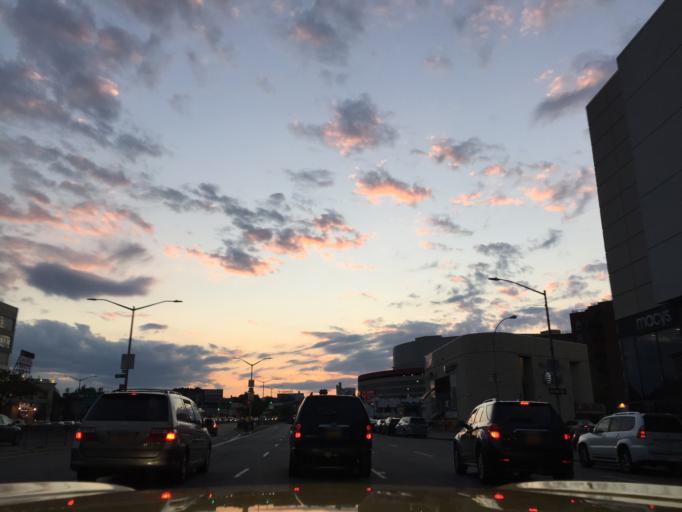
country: US
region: New York
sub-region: Queens County
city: Borough of Queens
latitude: 40.7341
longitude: -73.8716
